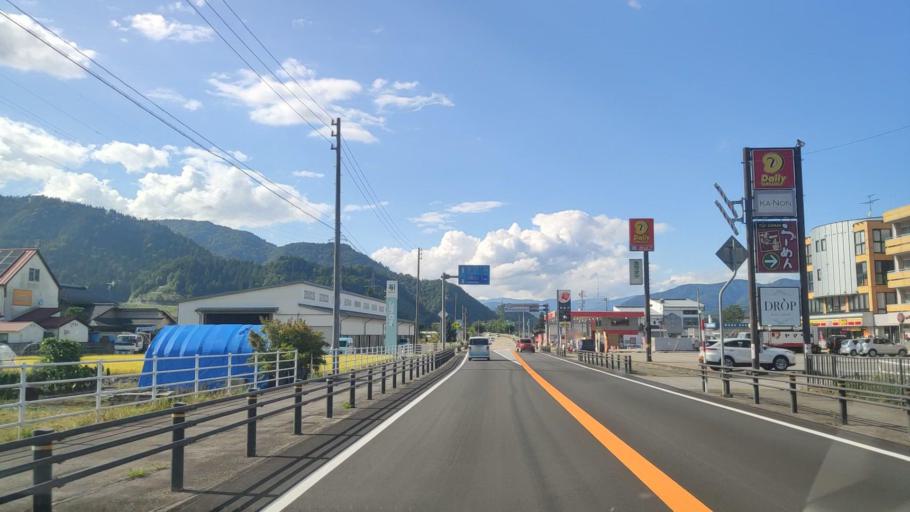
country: JP
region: Gifu
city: Takayama
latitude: 36.2272
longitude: 137.1866
